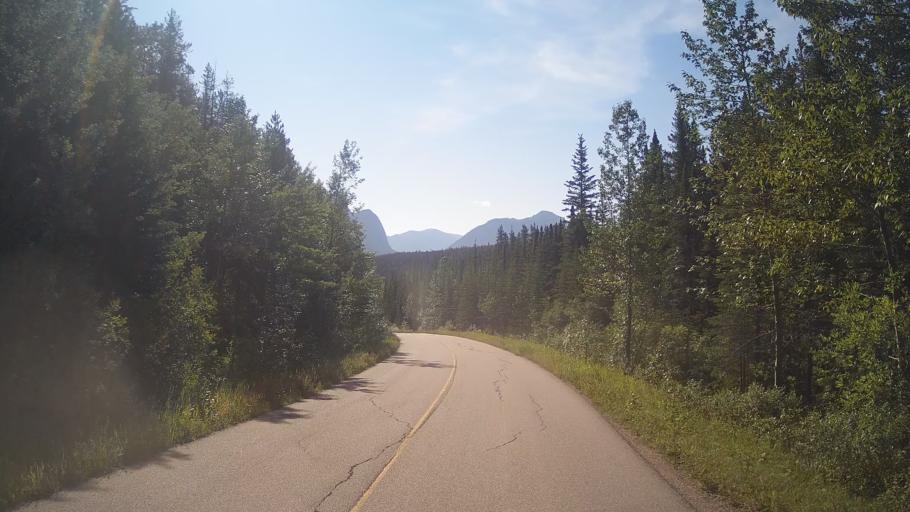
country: CA
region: Alberta
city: Jasper Park Lodge
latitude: 53.1788
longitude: -117.8646
